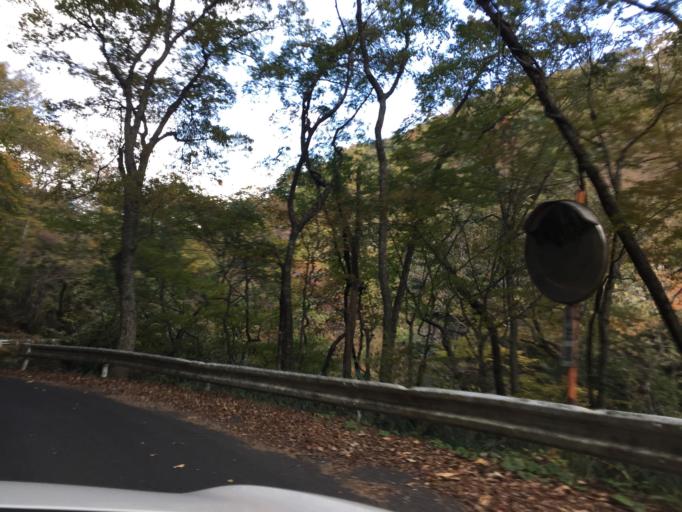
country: JP
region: Fukushima
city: Iwaki
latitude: 37.2195
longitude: 140.7567
